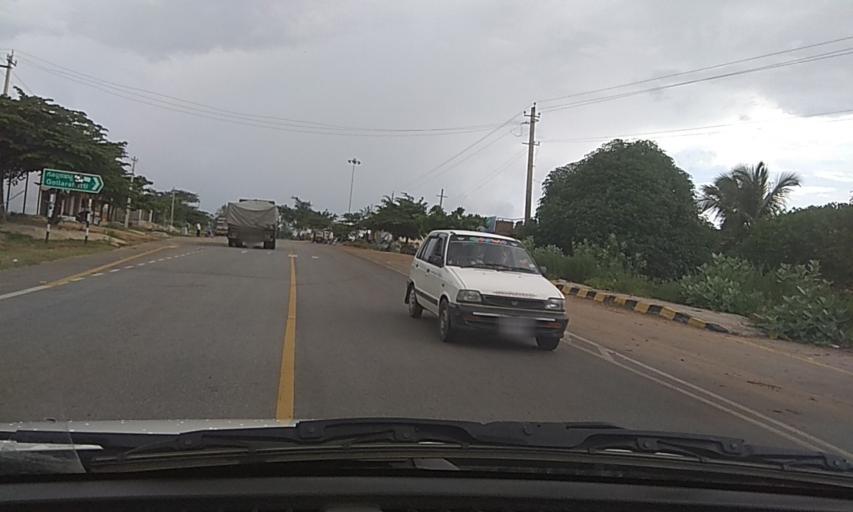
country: IN
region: Karnataka
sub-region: Tumkur
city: Kunigal
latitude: 12.8751
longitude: 77.0408
